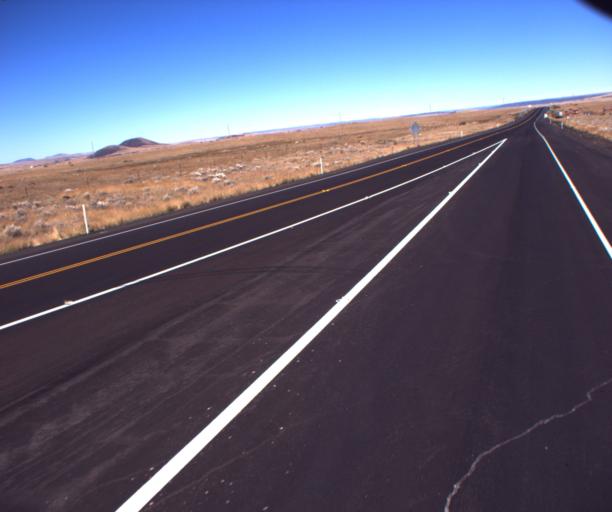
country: US
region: Arizona
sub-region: Apache County
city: Springerville
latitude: 34.1748
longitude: -109.3175
